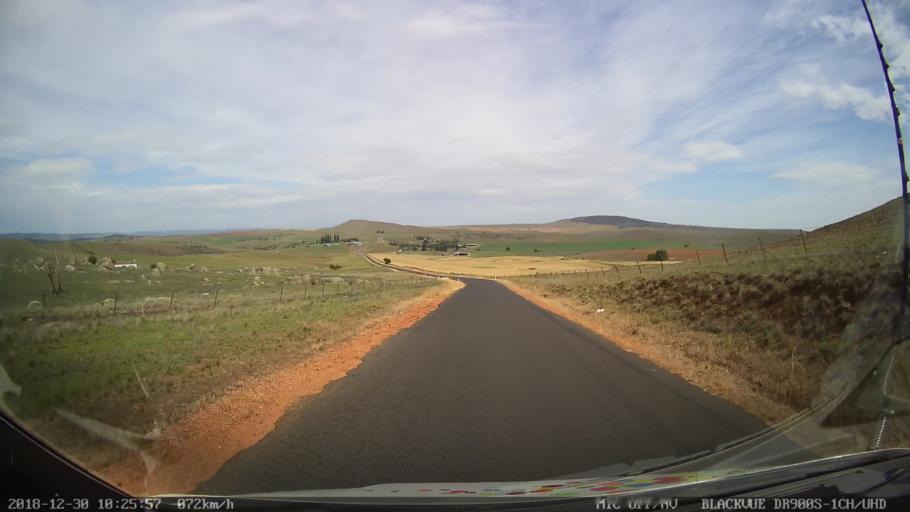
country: AU
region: New South Wales
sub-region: Snowy River
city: Berridale
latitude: -36.5210
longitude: 148.9530
